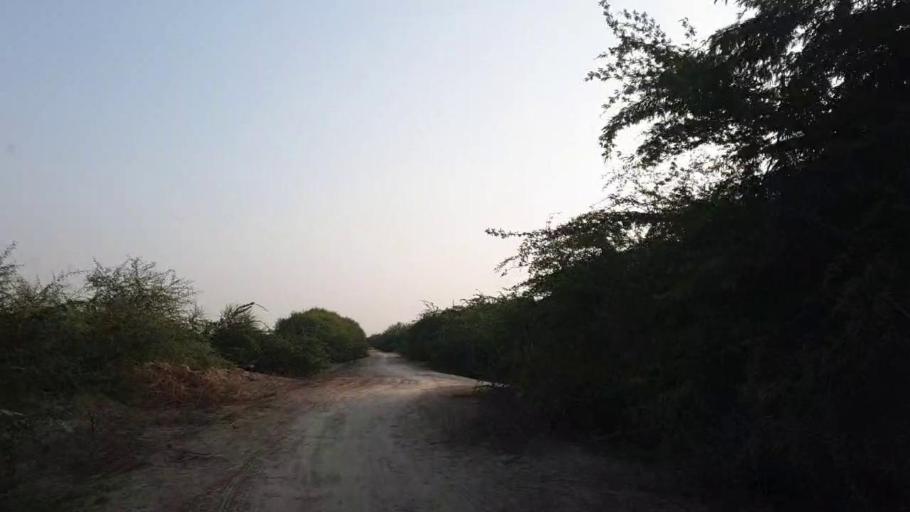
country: PK
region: Sindh
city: Kario
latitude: 24.8729
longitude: 68.6207
